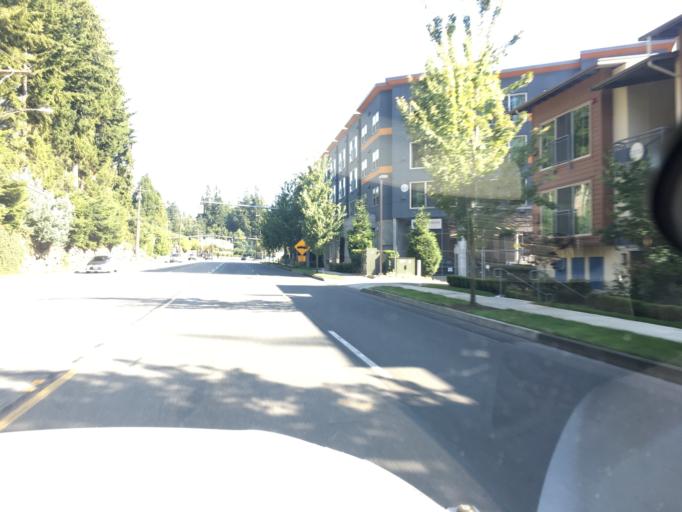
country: US
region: Washington
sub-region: Snohomish County
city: Esperance
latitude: 47.7899
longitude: -122.3562
